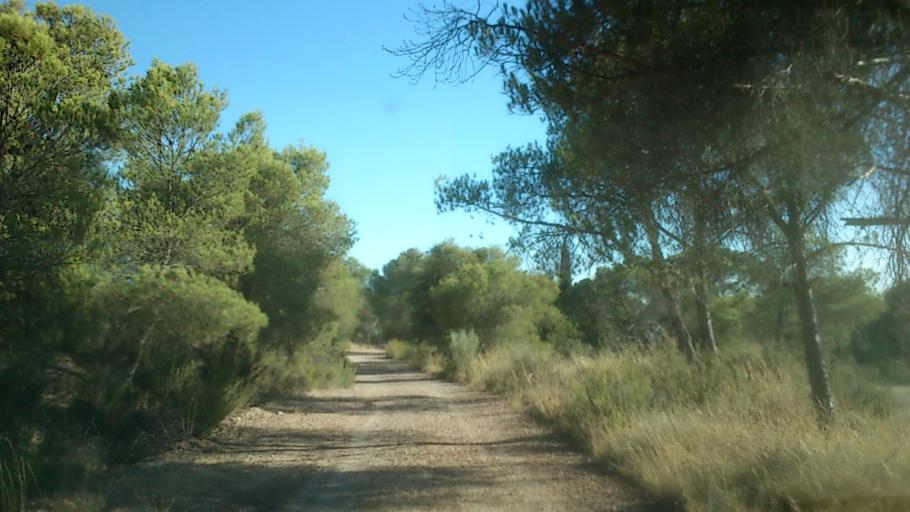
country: ES
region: Aragon
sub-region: Provincia de Zaragoza
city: San Mateo de Gallego
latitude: 41.7740
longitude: -0.7197
